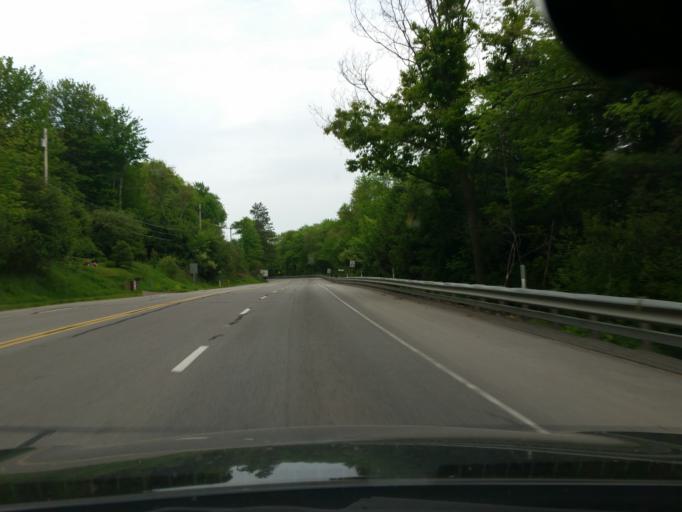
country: US
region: Pennsylvania
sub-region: Elk County
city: Ridgway
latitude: 41.4162
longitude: -78.7149
